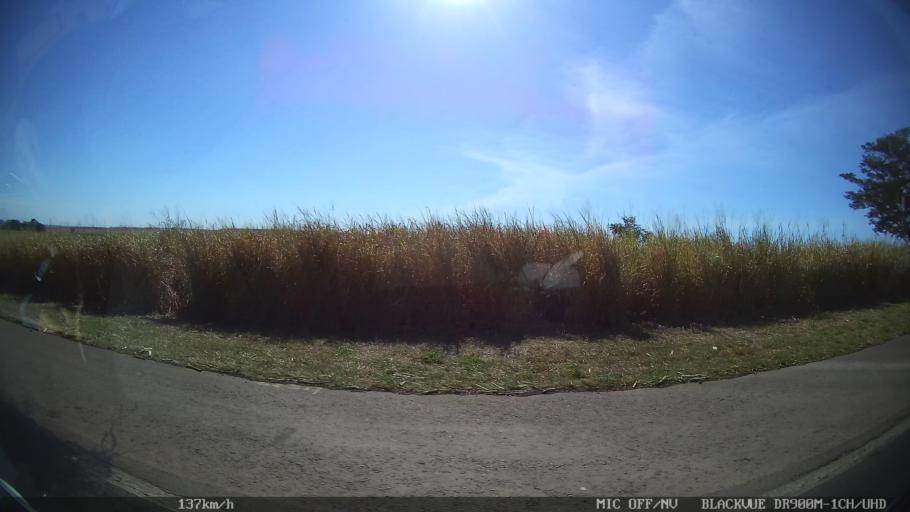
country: BR
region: Sao Paulo
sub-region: Olimpia
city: Olimpia
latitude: -20.6768
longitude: -48.8876
